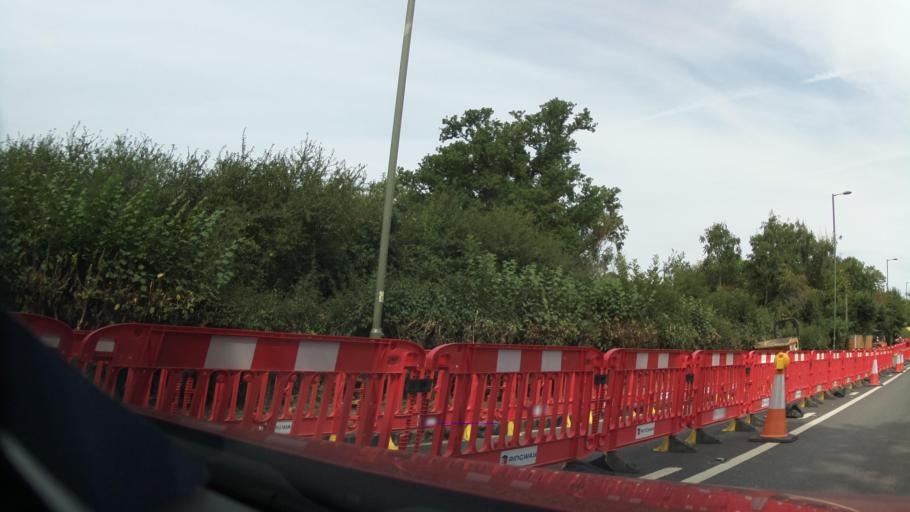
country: GB
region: England
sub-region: Surrey
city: Salfords
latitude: 51.1841
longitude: -0.1957
